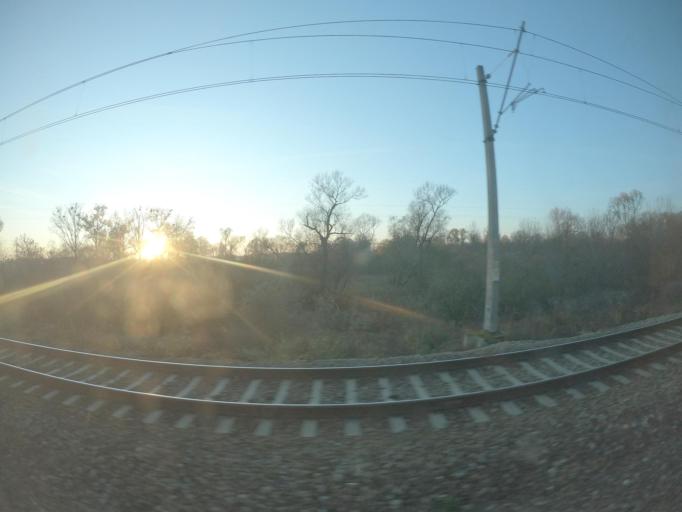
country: PL
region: Lubusz
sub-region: Powiat gorzowski
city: Kostrzyn nad Odra
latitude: 52.5764
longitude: 14.6439
